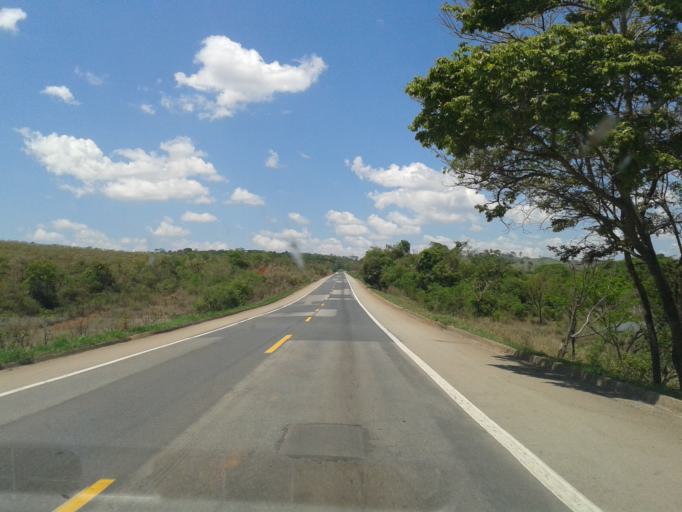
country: BR
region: Minas Gerais
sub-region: Ibia
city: Ibia
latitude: -19.5684
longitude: -46.6472
